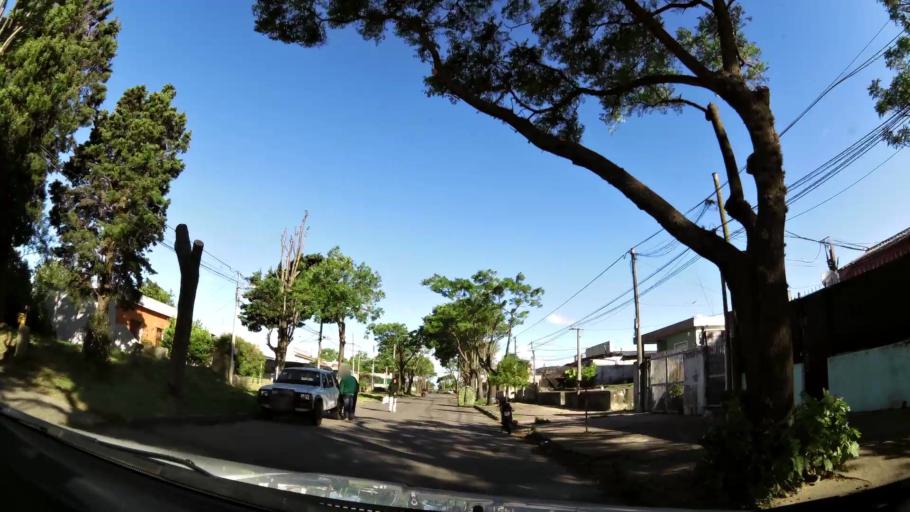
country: UY
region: Montevideo
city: Montevideo
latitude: -34.8422
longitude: -56.2396
